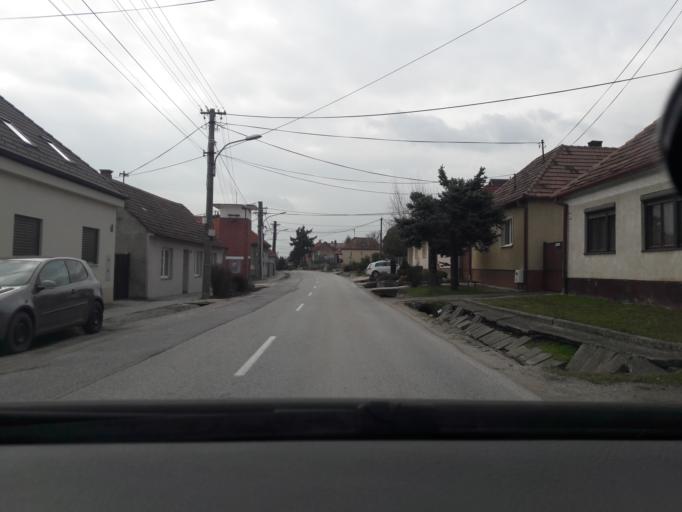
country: SK
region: Trnavsky
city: Smolenice
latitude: 48.4638
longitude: 17.4375
